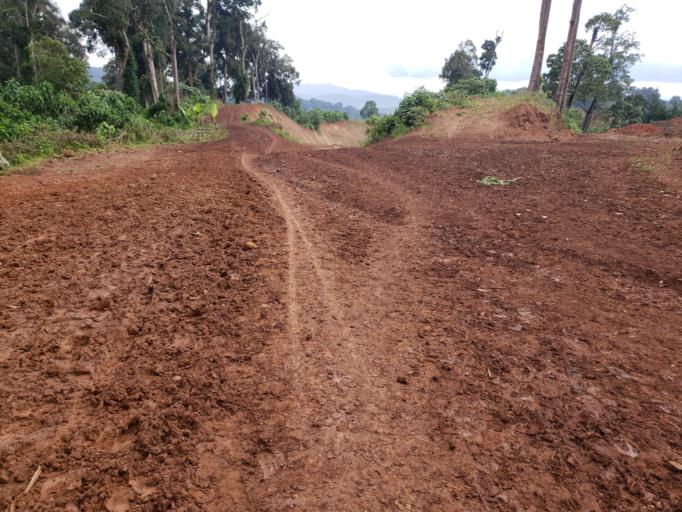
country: ET
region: Oromiya
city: Dodola
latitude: 6.5508
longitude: 39.4226
